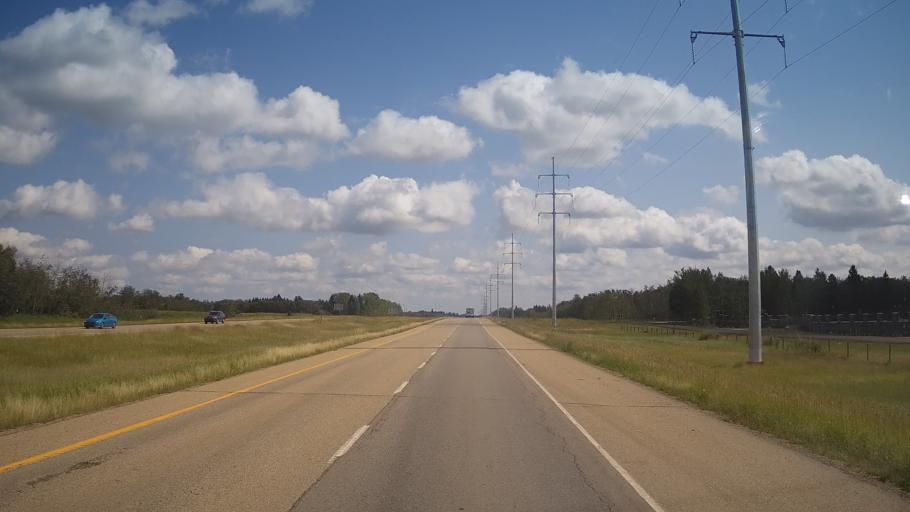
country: CA
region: Alberta
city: Sherwood Park
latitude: 53.4447
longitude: -113.2326
